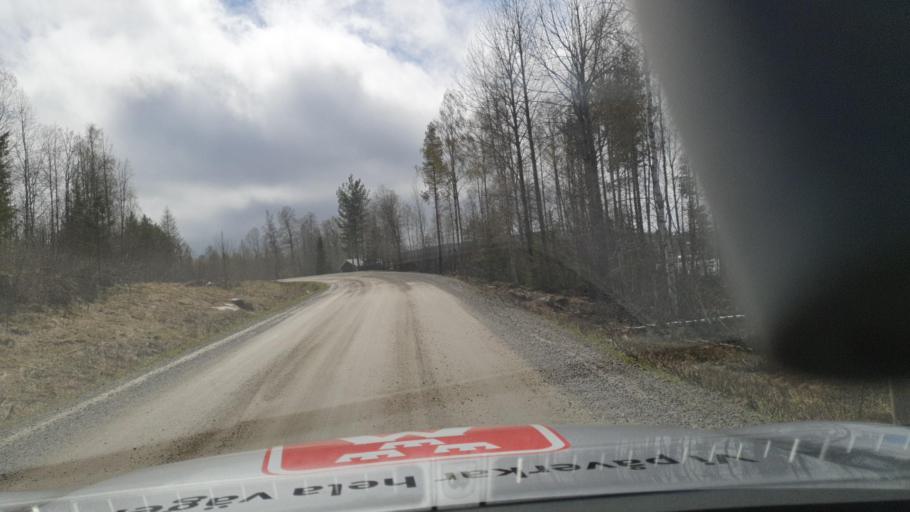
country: SE
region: Vaesterbotten
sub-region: Bjurholms Kommun
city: Bjurholm
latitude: 63.6921
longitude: 18.9577
